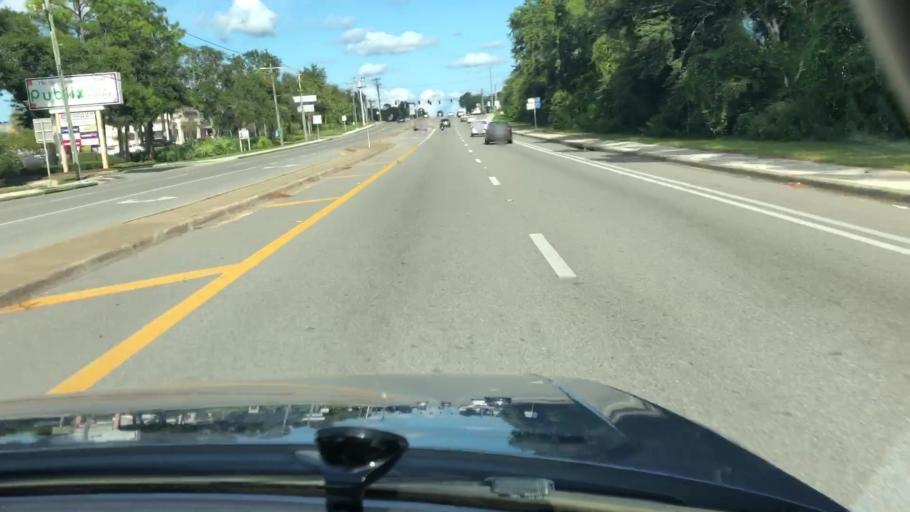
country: US
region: Florida
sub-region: Volusia County
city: South Daytona
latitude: 29.1698
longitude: -81.0415
